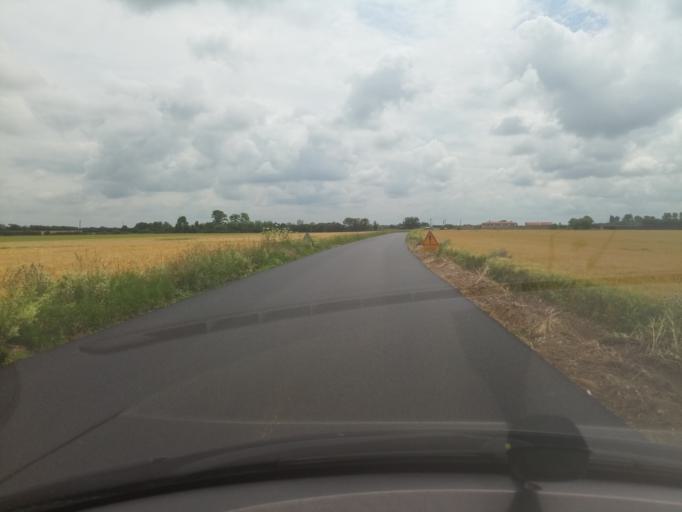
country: FR
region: Poitou-Charentes
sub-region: Departement de la Charente-Maritime
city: Saint-Jean-de-Liversay
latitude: 46.2720
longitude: -0.9004
